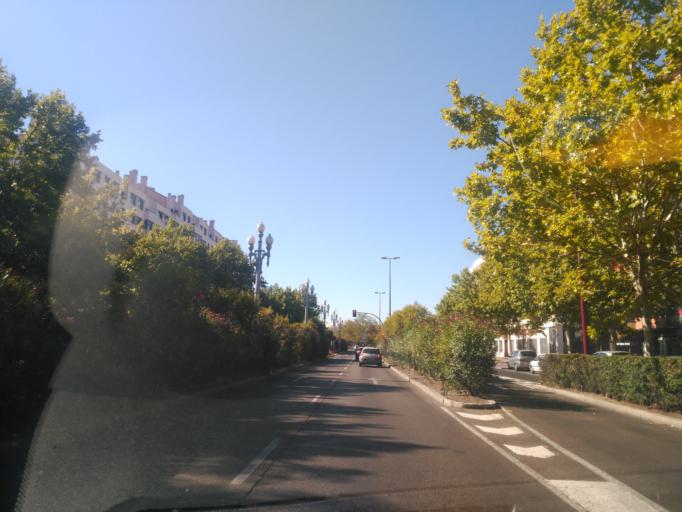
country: ES
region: Castille and Leon
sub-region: Provincia de Valladolid
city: Valladolid
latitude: 41.6246
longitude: -4.7467
